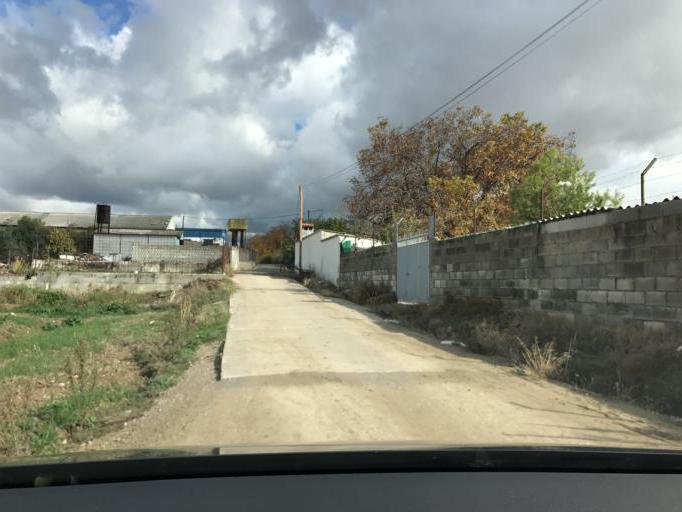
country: ES
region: Andalusia
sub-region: Provincia de Granada
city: Maracena
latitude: 37.2149
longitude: -3.6429
